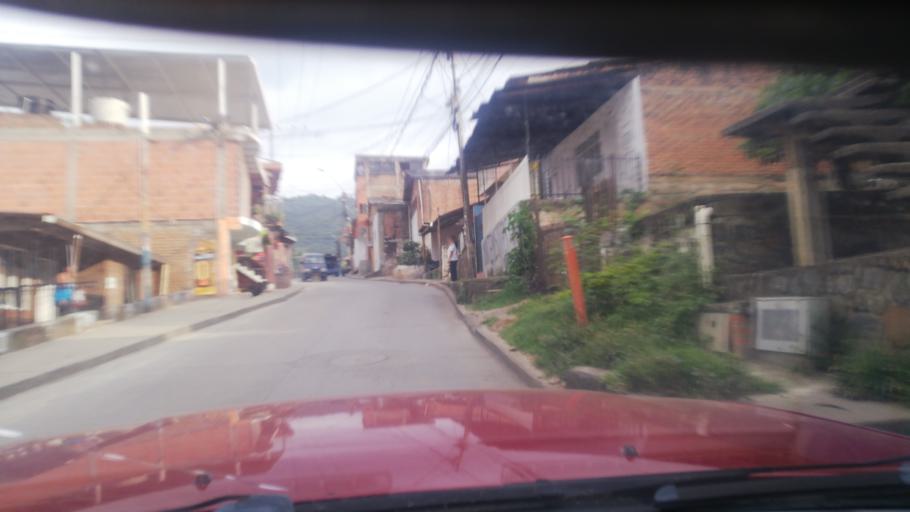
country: CO
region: Valle del Cauca
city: Cali
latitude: 3.4833
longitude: -76.5527
